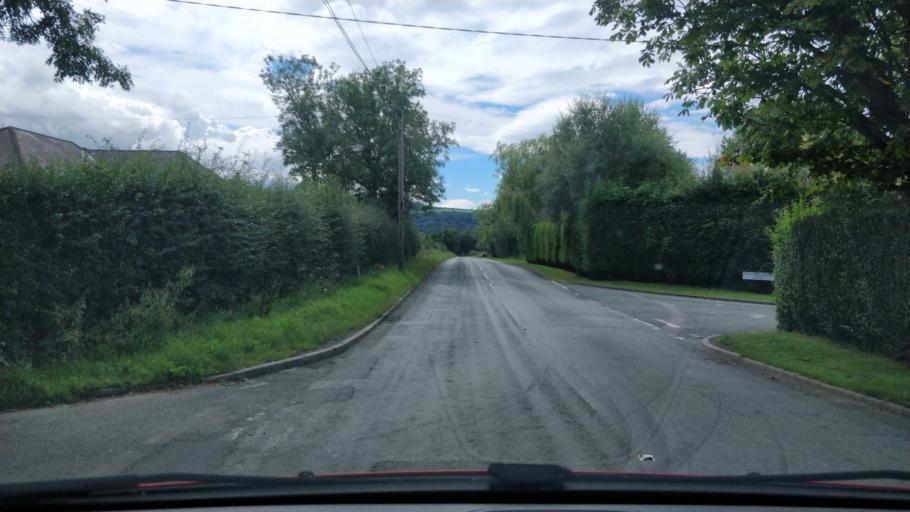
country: GB
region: Wales
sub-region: County of Flintshire
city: Hope
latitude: 53.1268
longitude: -3.0283
